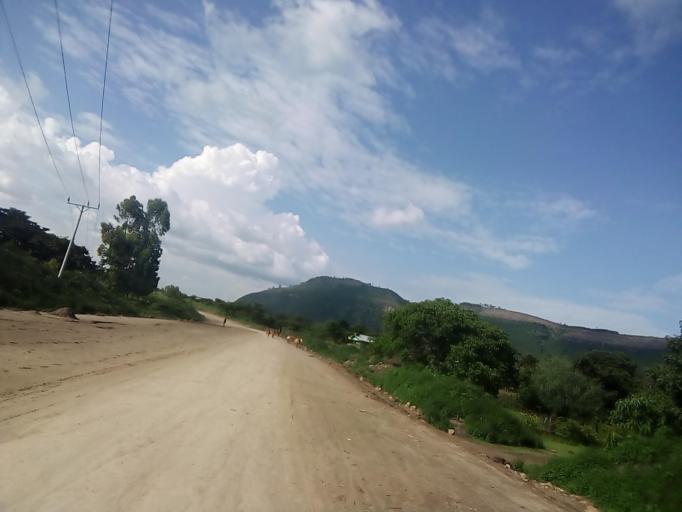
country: ET
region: Southern Nations, Nationalities, and People's Region
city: K'olito
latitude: 7.6217
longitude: 38.0639
